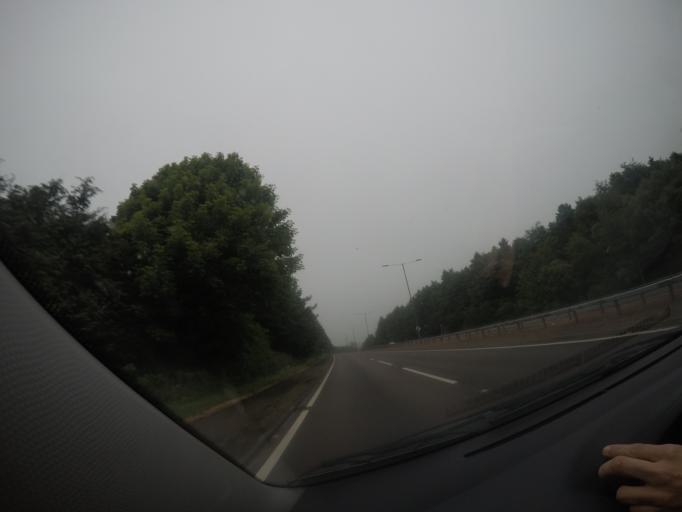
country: GB
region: Scotland
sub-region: Dundee City
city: Dundee
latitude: 56.5295
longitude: -2.9448
